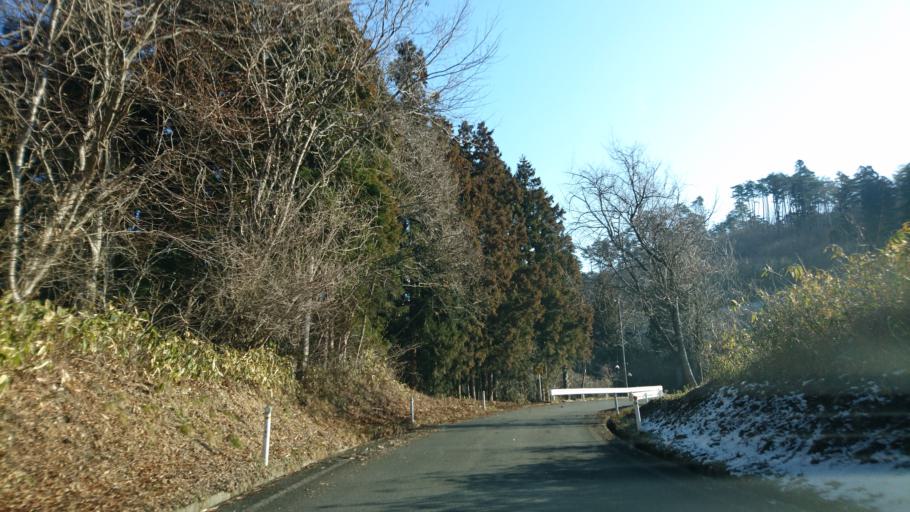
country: JP
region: Iwate
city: Ichinoseki
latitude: 38.9184
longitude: 141.2865
